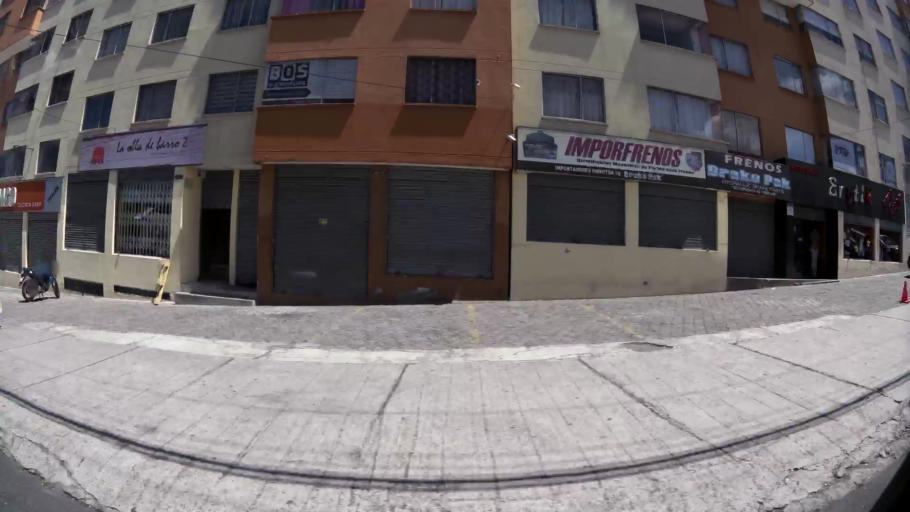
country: EC
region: Pichincha
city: Quito
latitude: -0.1302
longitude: -78.4815
